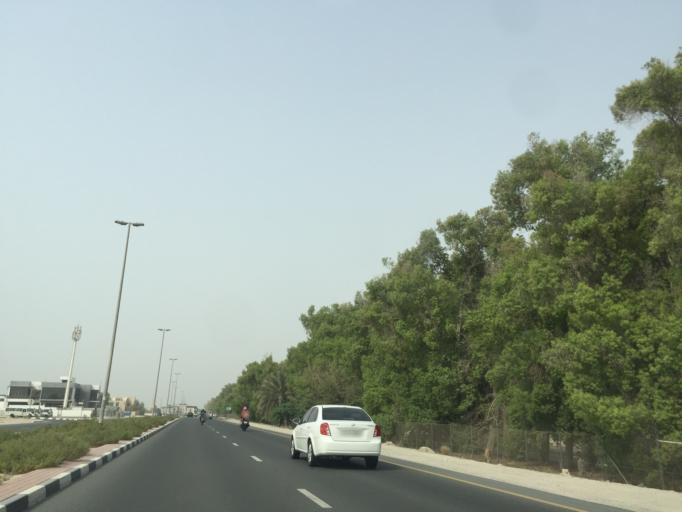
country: AE
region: Dubai
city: Dubai
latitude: 25.1251
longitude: 55.1866
